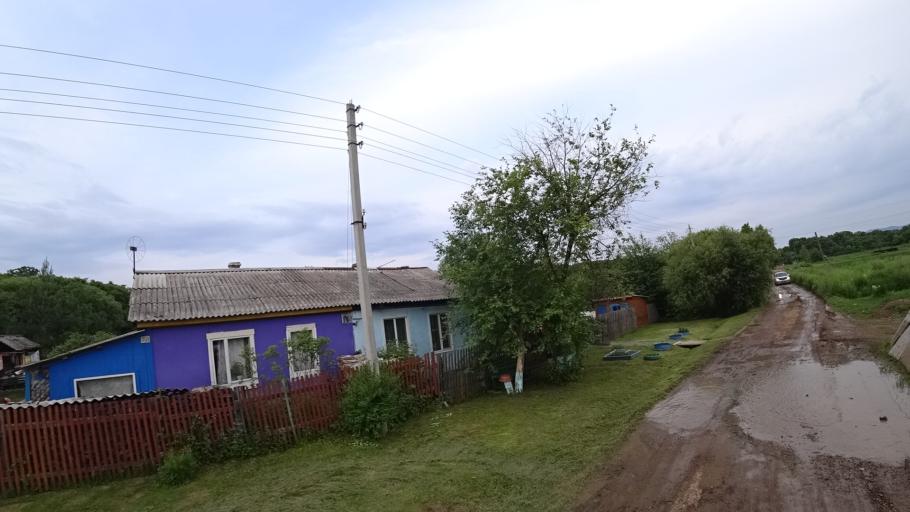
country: RU
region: Primorskiy
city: Novosysoyevka
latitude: 44.2367
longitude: 133.3795
